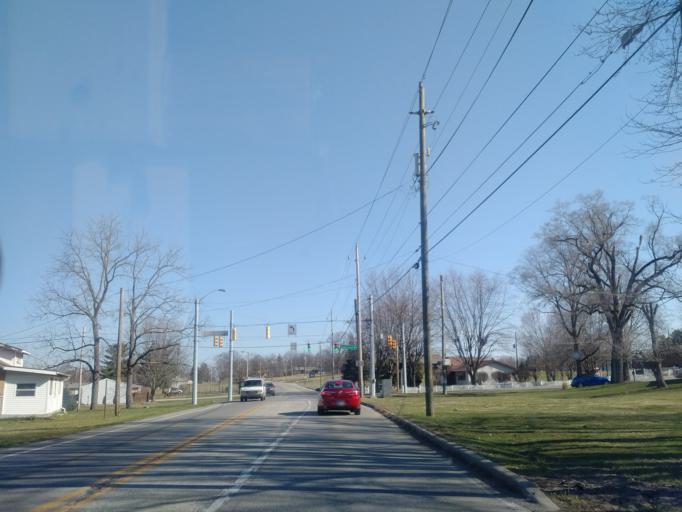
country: US
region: Indiana
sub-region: Marion County
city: Southport
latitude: 39.6782
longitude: -86.1759
